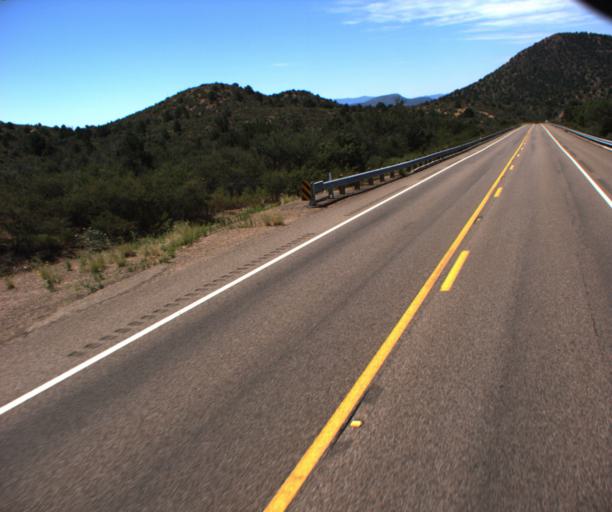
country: US
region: Arizona
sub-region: Gila County
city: Globe
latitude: 33.6172
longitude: -110.6034
